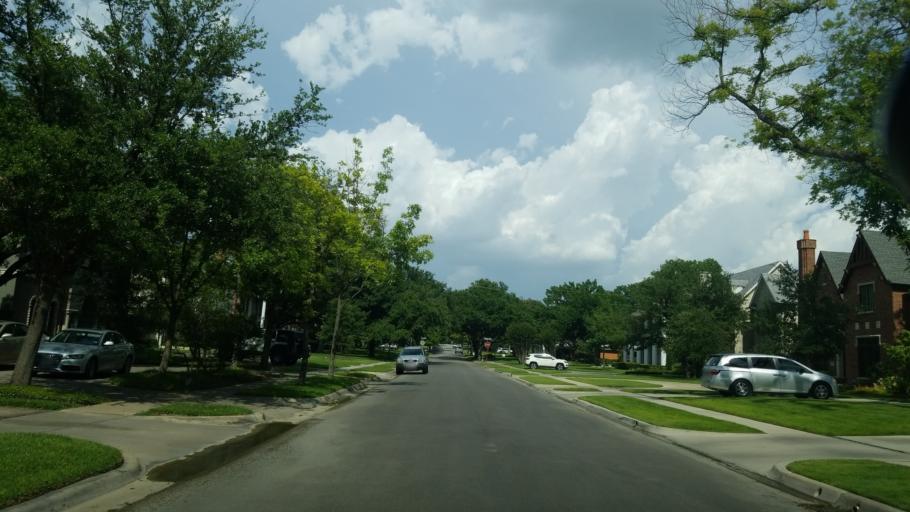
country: US
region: Texas
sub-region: Dallas County
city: University Park
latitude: 32.8644
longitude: -96.7970
